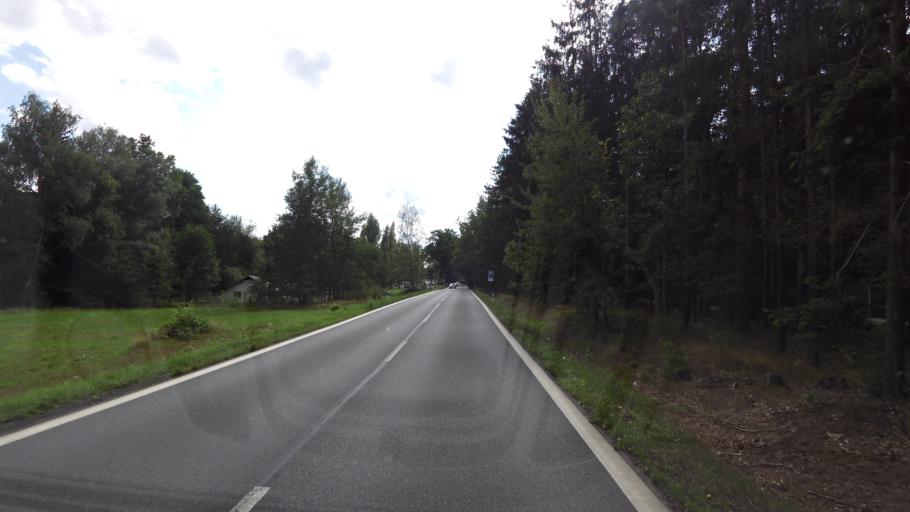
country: CZ
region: Plzensky
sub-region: Okres Domazlice
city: Klenci pod Cerchovem
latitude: 49.4075
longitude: 12.8626
